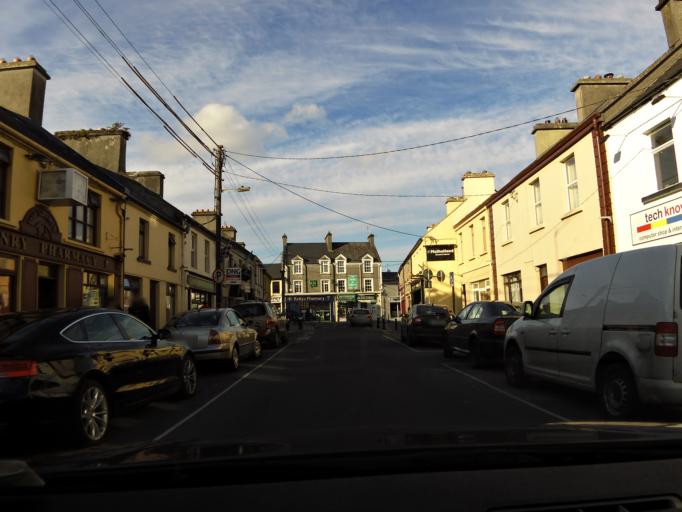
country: IE
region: Connaught
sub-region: County Galway
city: Athenry
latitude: 53.2986
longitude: -8.7481
